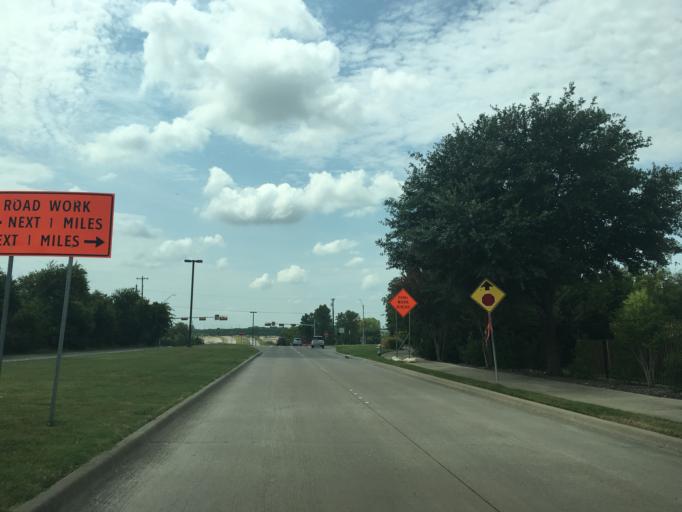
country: US
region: Texas
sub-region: Rockwall County
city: Rockwall
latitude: 32.9446
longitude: -96.4424
